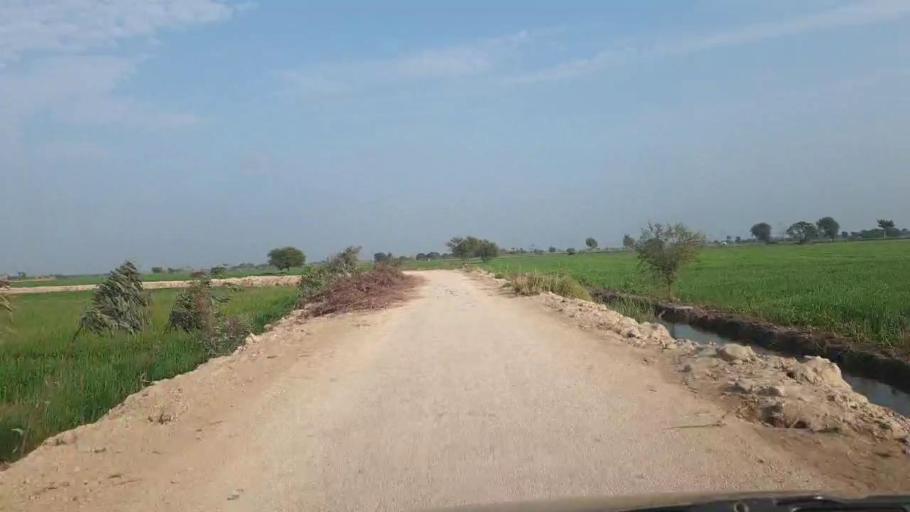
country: PK
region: Sindh
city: Shahdadpur
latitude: 25.8755
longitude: 68.7020
